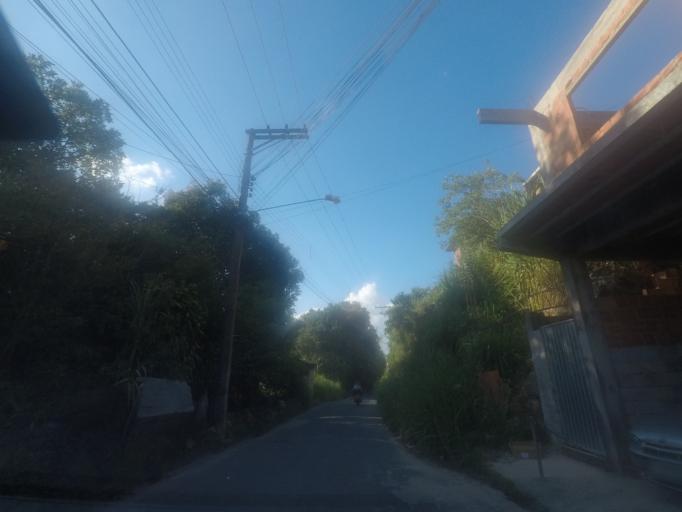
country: BR
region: Rio de Janeiro
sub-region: Petropolis
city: Petropolis
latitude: -22.4936
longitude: -43.1496
